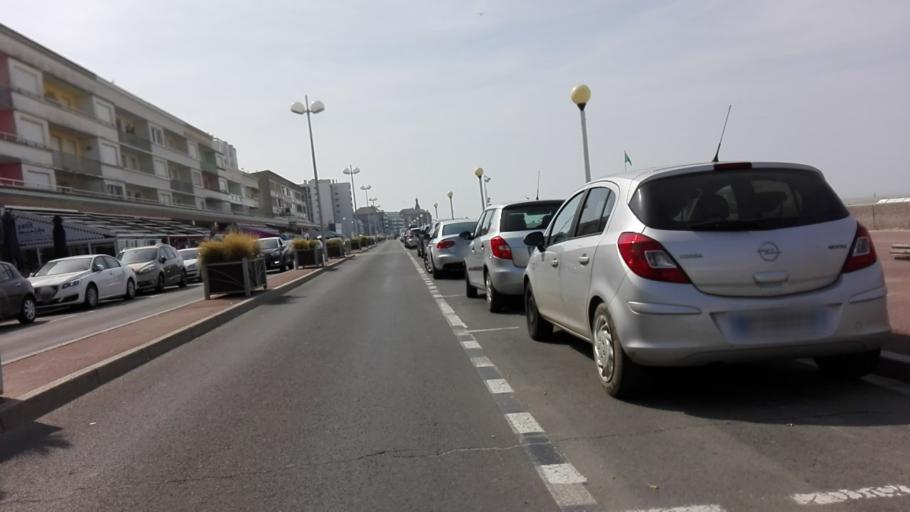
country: FR
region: Nord-Pas-de-Calais
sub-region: Departement du Pas-de-Calais
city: Berck-Plage
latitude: 50.4071
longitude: 1.5601
